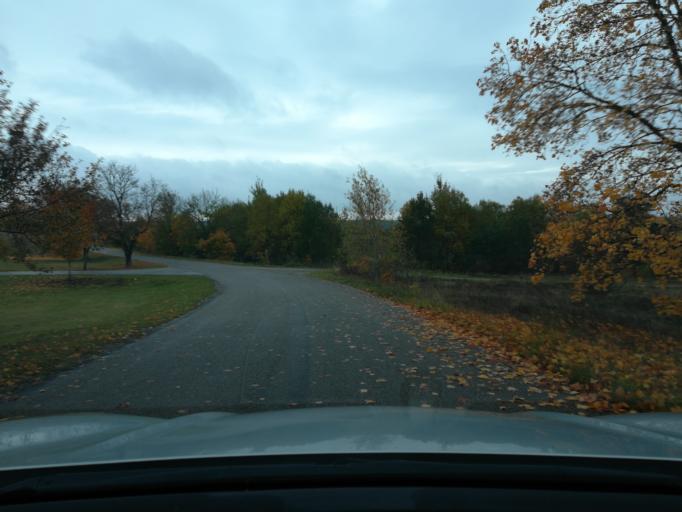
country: EE
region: Ida-Virumaa
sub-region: Johvi vald
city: Johvi
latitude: 59.1940
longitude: 27.5416
